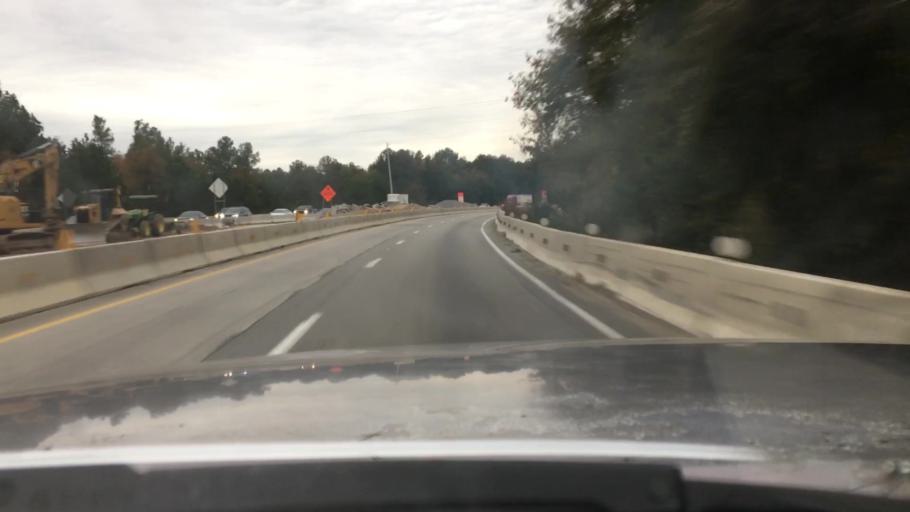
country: US
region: South Carolina
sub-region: Lexington County
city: Lexington
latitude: 33.9717
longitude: -81.1980
